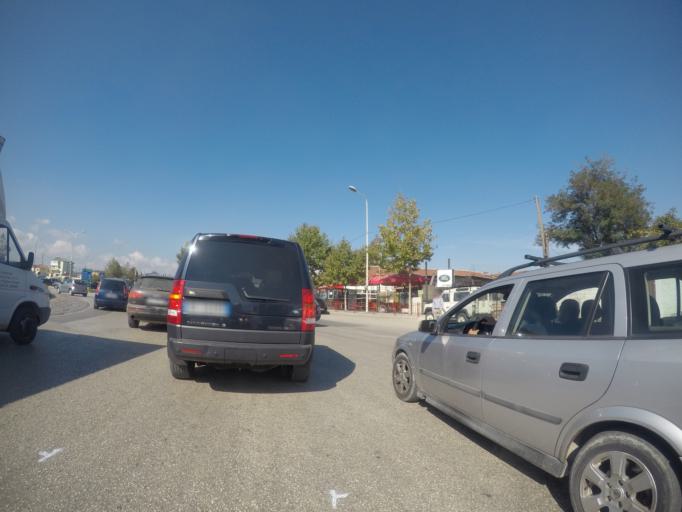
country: AL
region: Tirane
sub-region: Rrethi i Tiranes
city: Paskuqan
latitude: 41.3396
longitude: 19.7866
